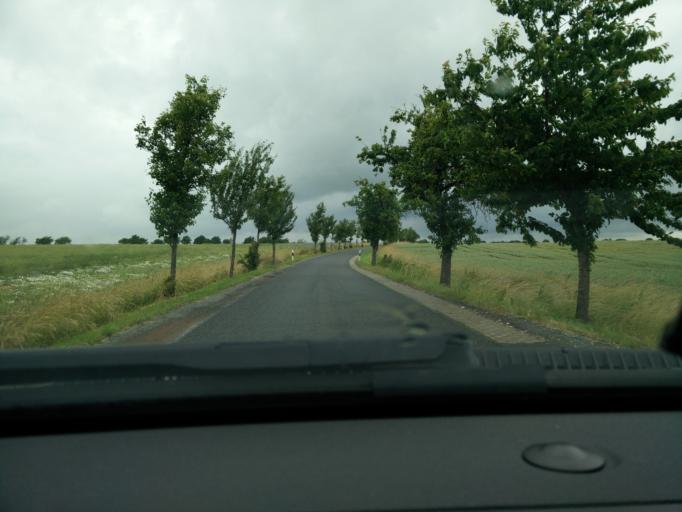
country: DE
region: Saxony
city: Bad Lausick
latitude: 51.1297
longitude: 12.6897
